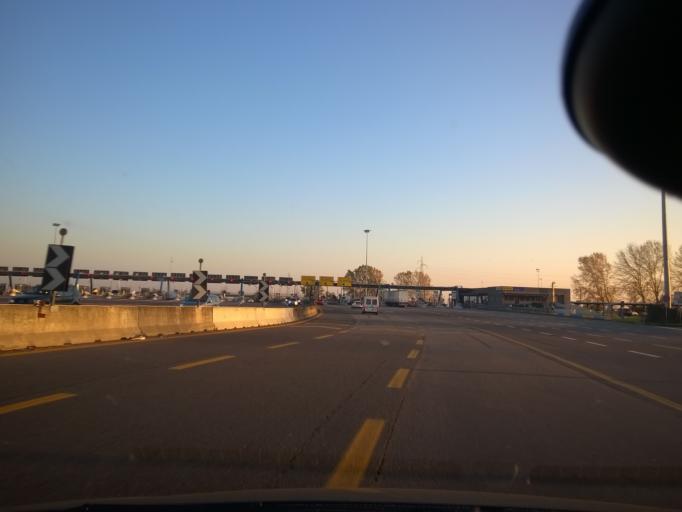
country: IT
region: Lombardy
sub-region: Citta metropolitana di Milano
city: Riozzo
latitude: 45.3498
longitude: 9.3087
